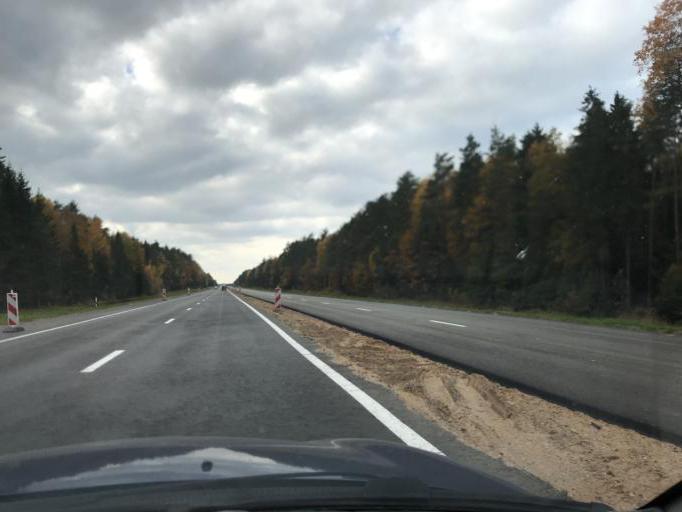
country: BY
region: Grodnenskaya
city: Lida
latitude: 53.8397
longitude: 25.1685
